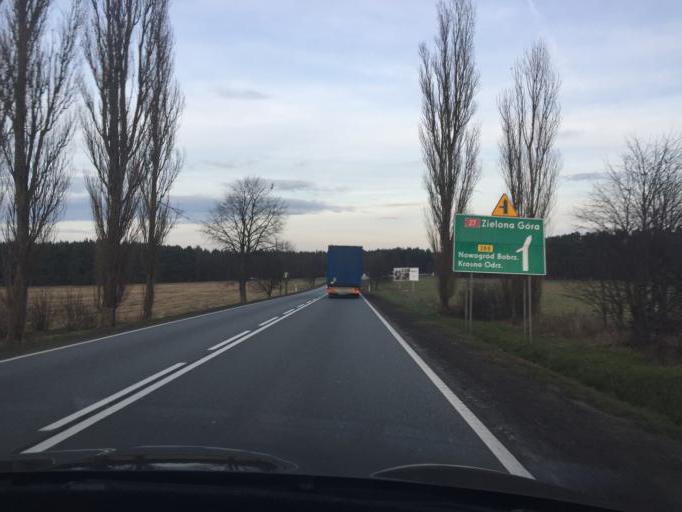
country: PL
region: Lubusz
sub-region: Powiat zielonogorski
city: Nowogrod Bobrzanski
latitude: 51.8081
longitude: 15.2615
